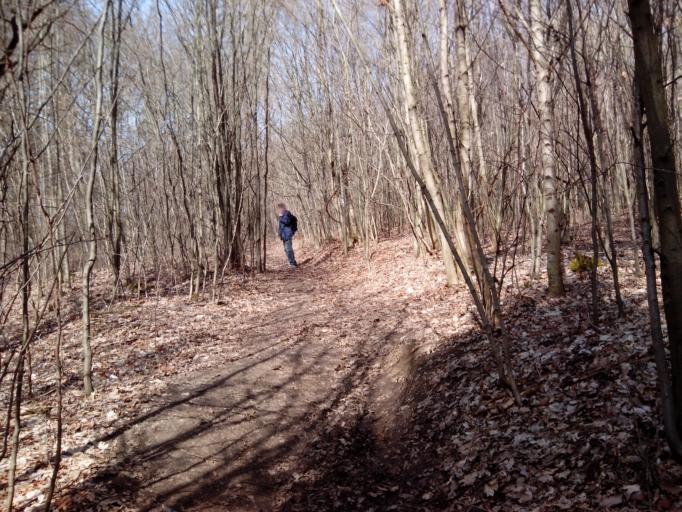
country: CZ
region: Central Bohemia
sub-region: Okres Beroun
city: Beroun
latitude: 49.9341
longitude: 14.1102
